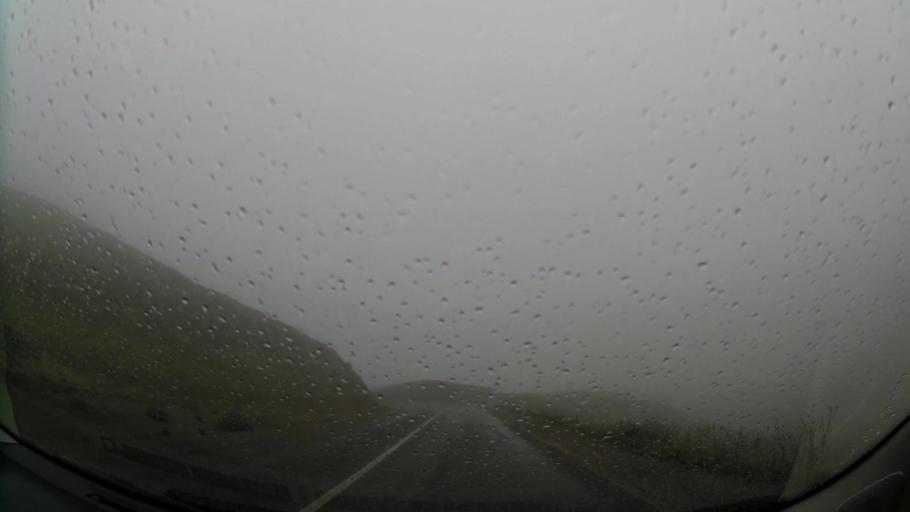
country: MA
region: Oriental
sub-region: Nador
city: Boudinar
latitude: 35.0968
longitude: -3.5331
